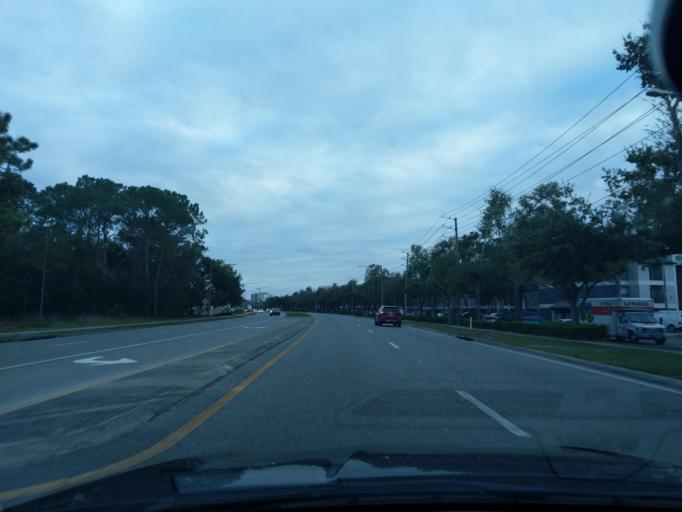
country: US
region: Florida
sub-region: Orange County
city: Doctor Phillips
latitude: 28.3954
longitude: -81.5055
